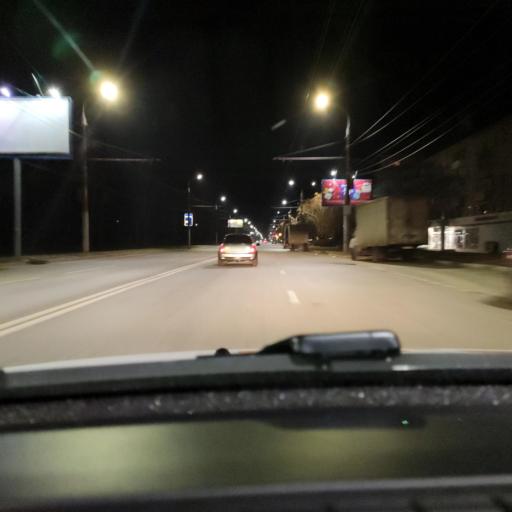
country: RU
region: Voronezj
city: Voronezh
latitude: 51.6545
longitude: 39.1338
